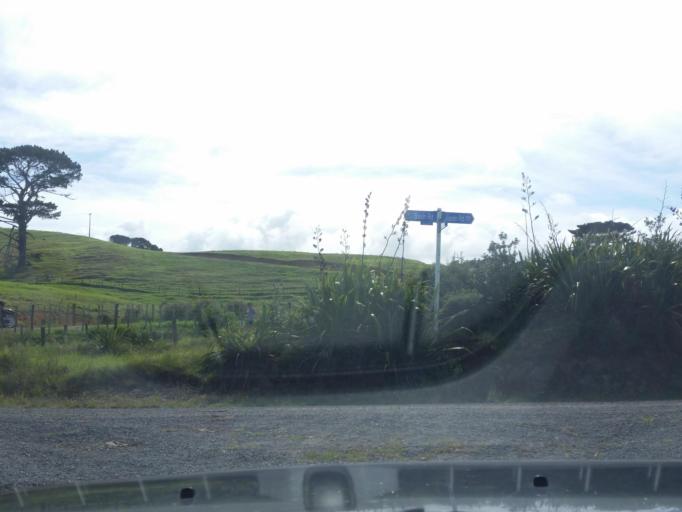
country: NZ
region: Northland
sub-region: Kaipara District
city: Dargaville
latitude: -35.9194
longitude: 173.7368
